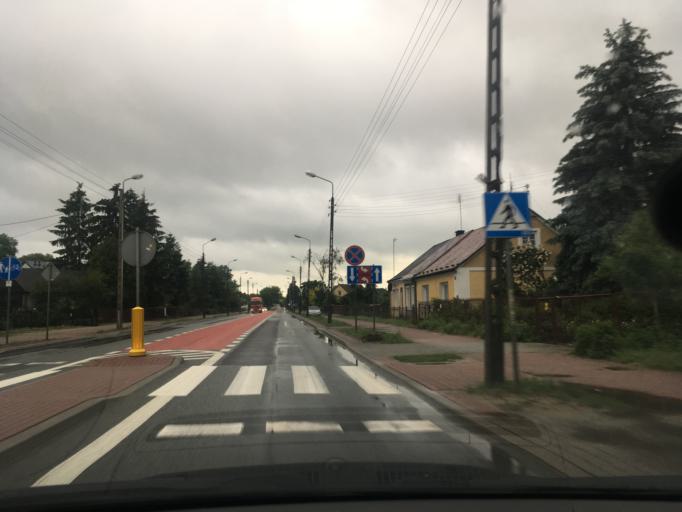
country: PL
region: Lublin Voivodeship
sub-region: Powiat rycki
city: Deblin
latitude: 51.5657
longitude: 21.8757
